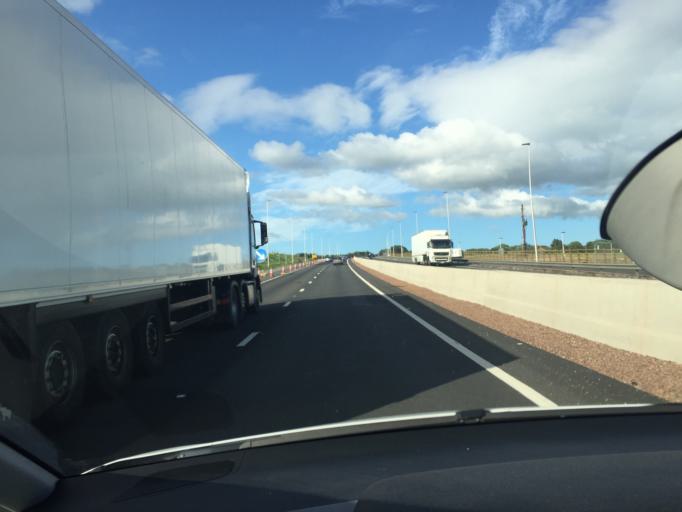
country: GB
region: Scotland
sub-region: South Lanarkshire
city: Bothwell
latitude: 55.8064
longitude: -4.0472
